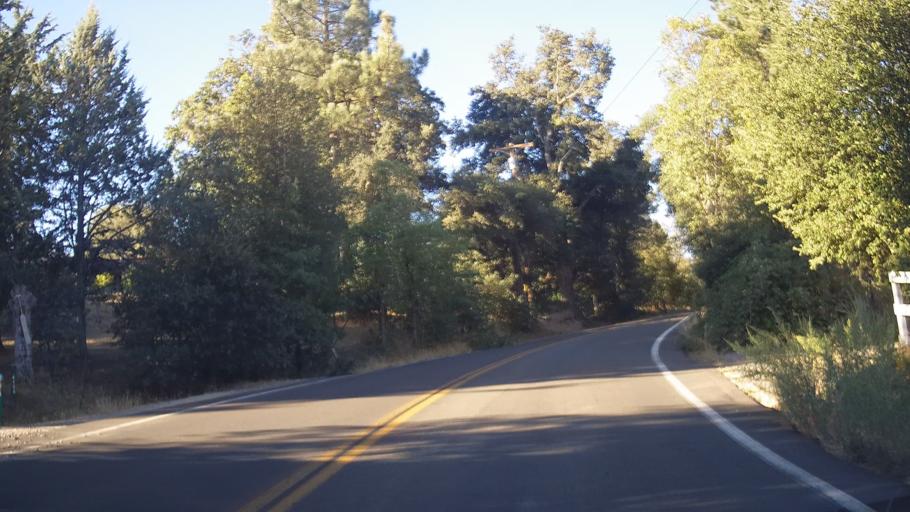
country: US
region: California
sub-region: San Diego County
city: Julian
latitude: 33.0516
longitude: -116.6205
